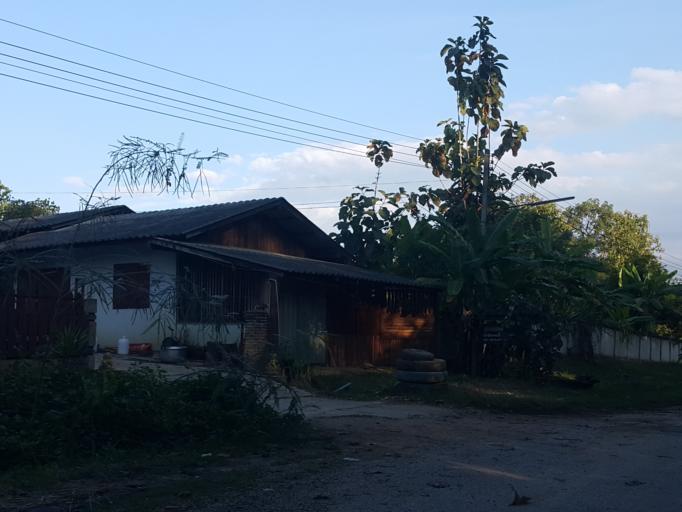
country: TH
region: Lampang
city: Lampang
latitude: 18.4208
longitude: 99.5529
